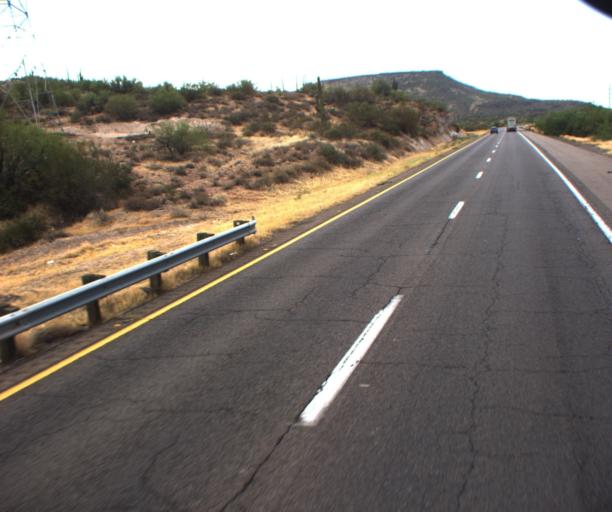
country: US
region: Arizona
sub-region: Maricopa County
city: New River
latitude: 33.9772
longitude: -112.1317
